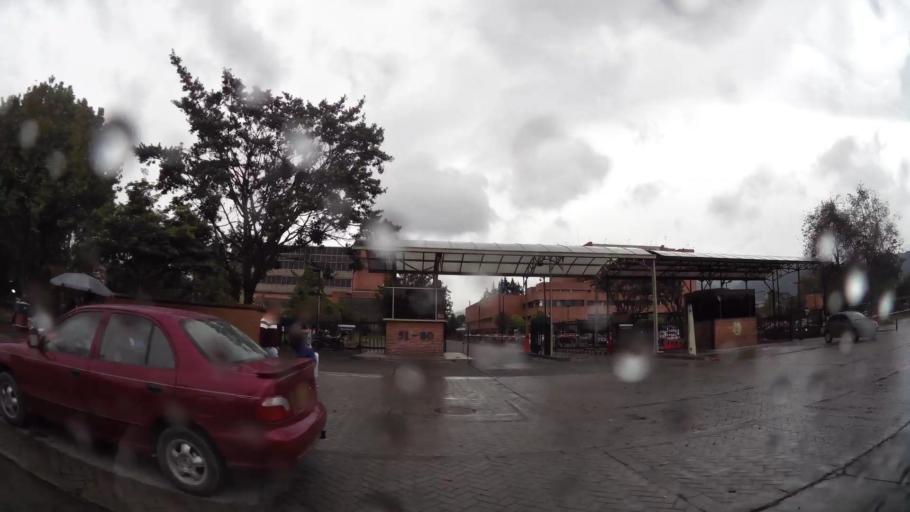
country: CO
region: Bogota D.C.
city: Bogota
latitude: 4.6425
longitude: -74.0958
